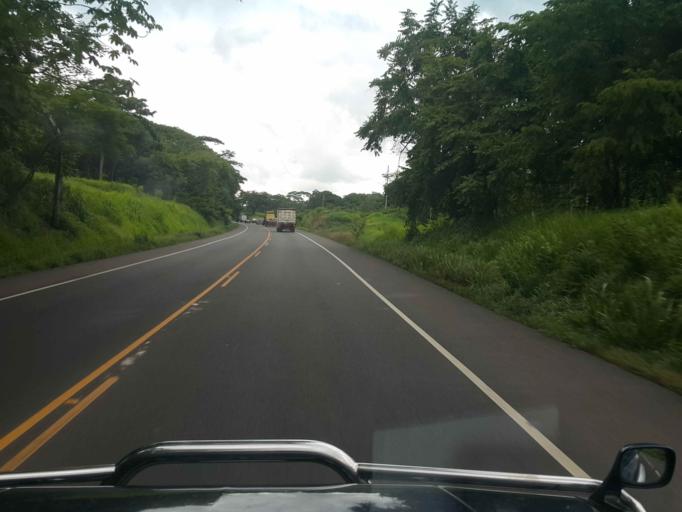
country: CR
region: Puntarenas
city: Esparza
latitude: 9.9001
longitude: -84.6583
